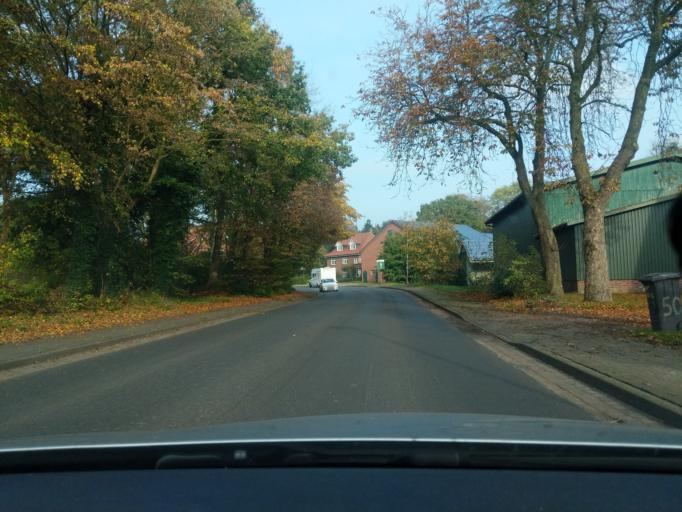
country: DE
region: Lower Saxony
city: Mittelstenahe
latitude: 53.6497
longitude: 9.0330
